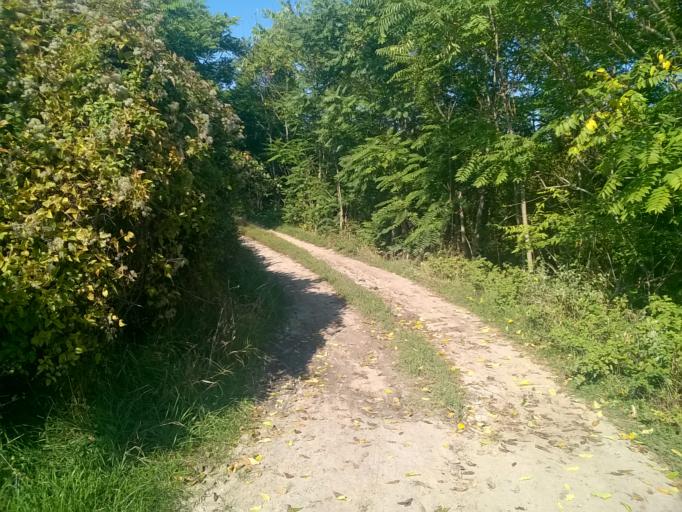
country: HU
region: Pest
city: Toekoel
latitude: 47.3402
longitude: 18.9454
